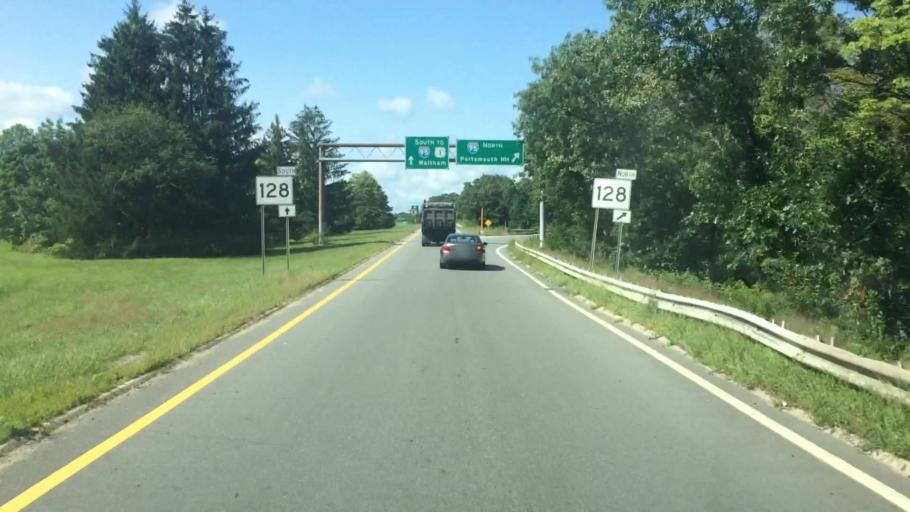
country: US
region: Massachusetts
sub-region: Essex County
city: South Peabody
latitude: 42.5162
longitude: -70.9918
